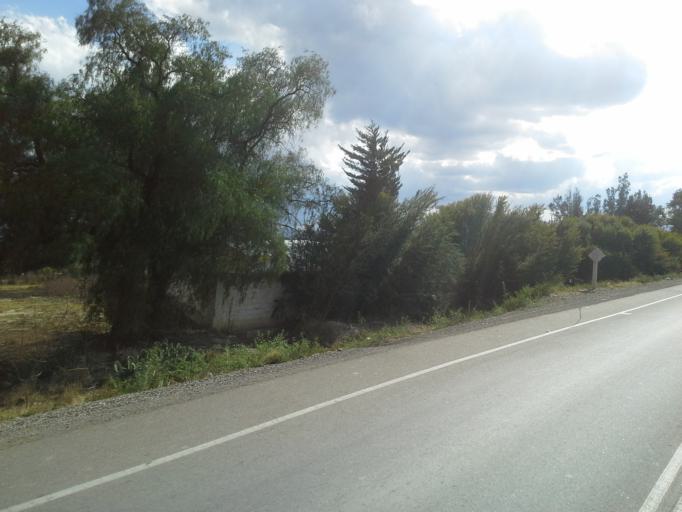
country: BO
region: Cochabamba
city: Tarata
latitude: -17.5445
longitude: -66.0069
